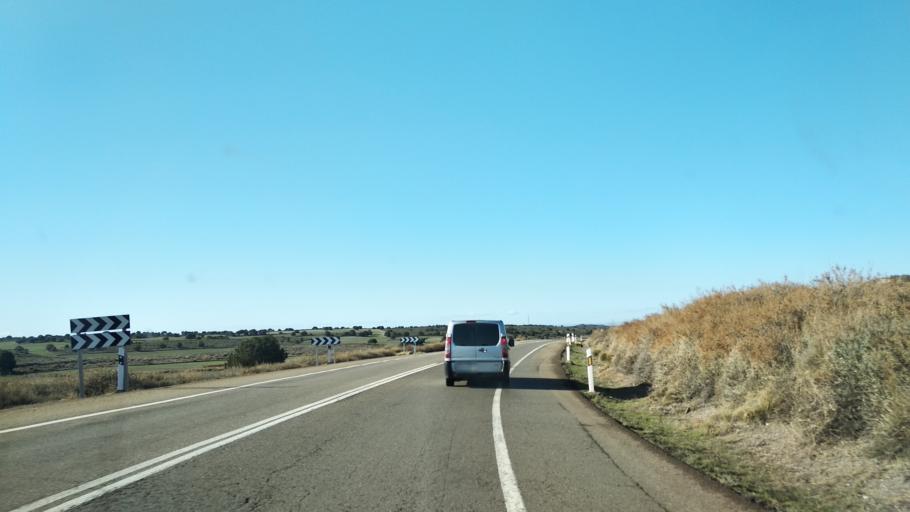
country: ES
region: Aragon
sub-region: Provincia de Zaragoza
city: Bujaraloz
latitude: 41.4939
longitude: -0.2302
